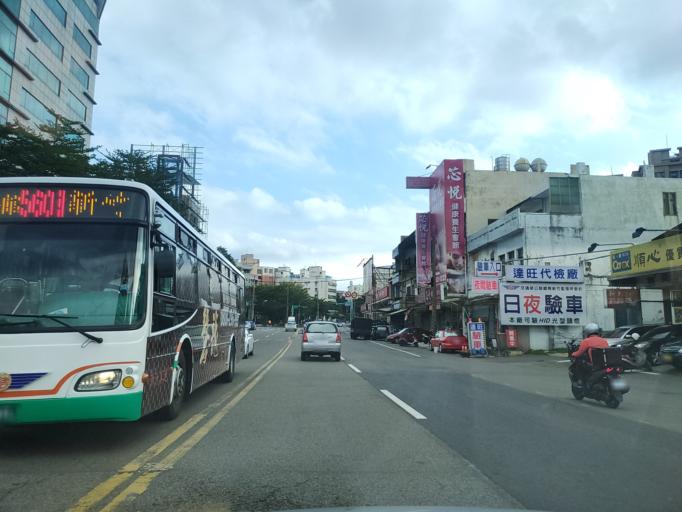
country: TW
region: Taiwan
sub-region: Hsinchu
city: Hsinchu
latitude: 24.8066
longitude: 120.9859
